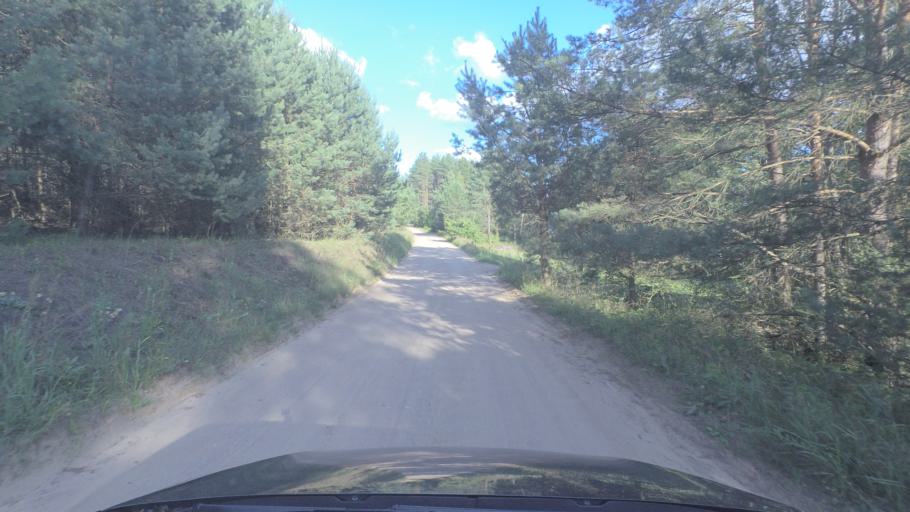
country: LT
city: Pabrade
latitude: 55.1396
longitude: 25.7126
